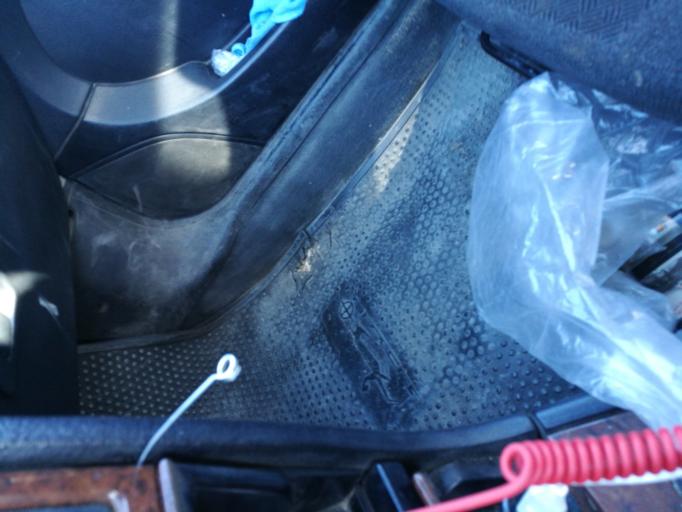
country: IR
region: Chahar Mahall va Bakhtiari
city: Farrokh Shahr
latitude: 32.3505
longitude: 51.1249
